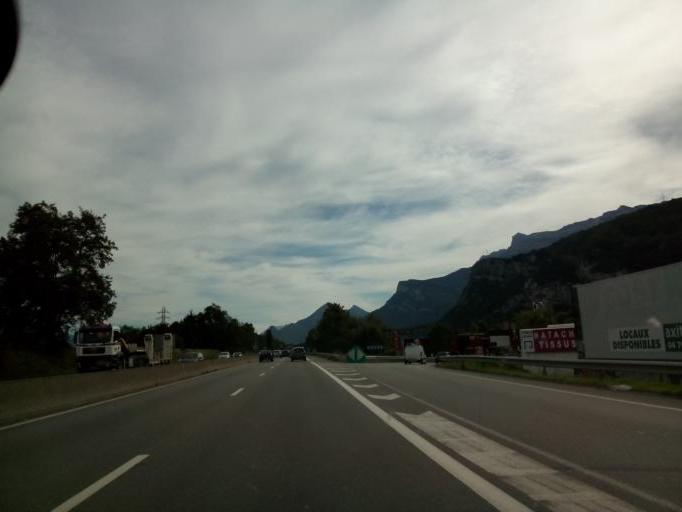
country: FR
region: Rhone-Alpes
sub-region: Departement de l'Isere
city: Seyssins
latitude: 45.1519
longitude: 5.6974
